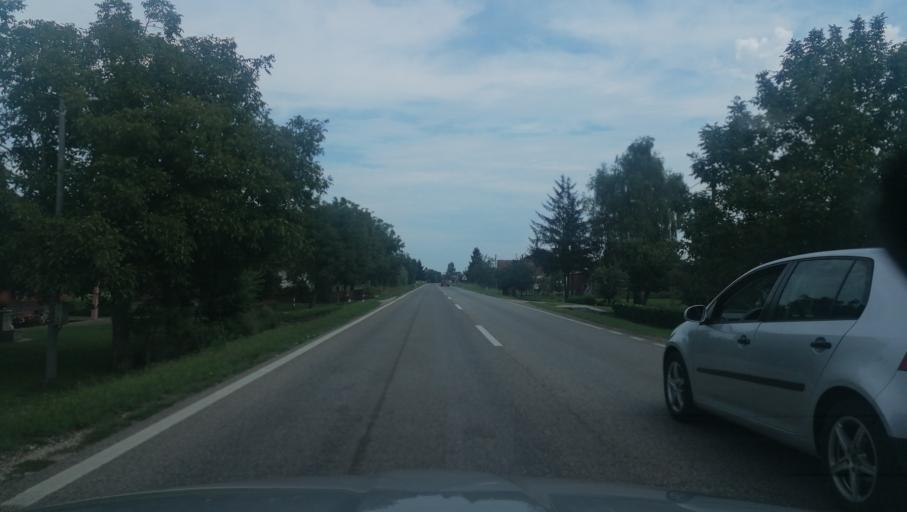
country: BA
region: Federation of Bosnia and Herzegovina
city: Odzak
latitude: 44.9660
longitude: 18.3341
